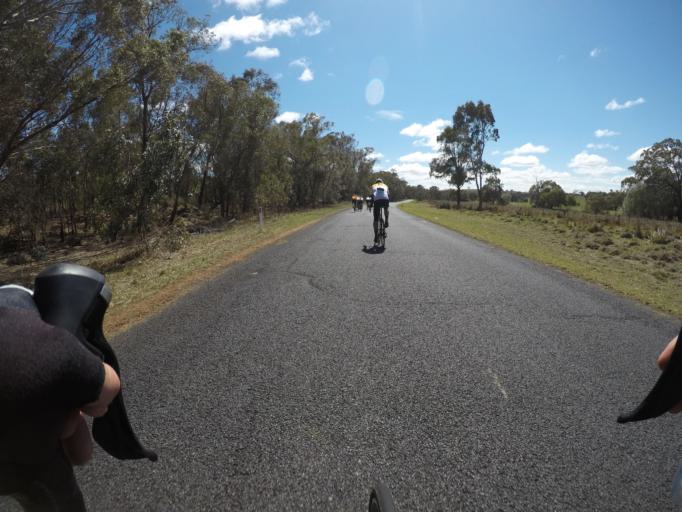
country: AU
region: New South Wales
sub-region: Dubbo Municipality
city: Dubbo
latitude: -32.5546
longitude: 148.5389
